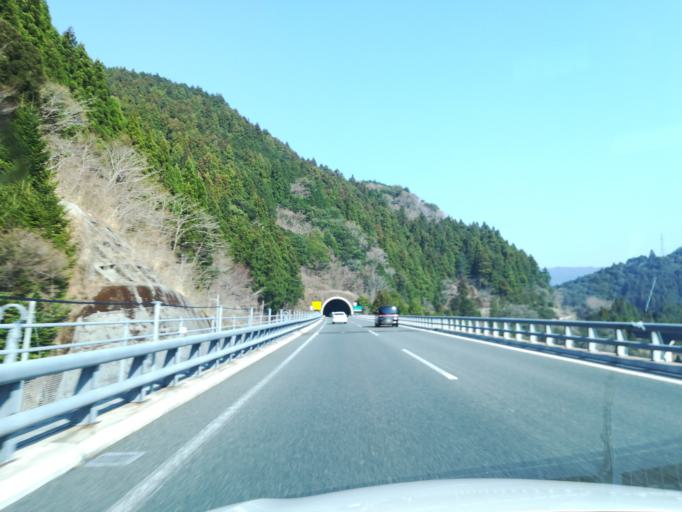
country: JP
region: Ehime
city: Kawanoecho
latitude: 33.8297
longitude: 133.6587
